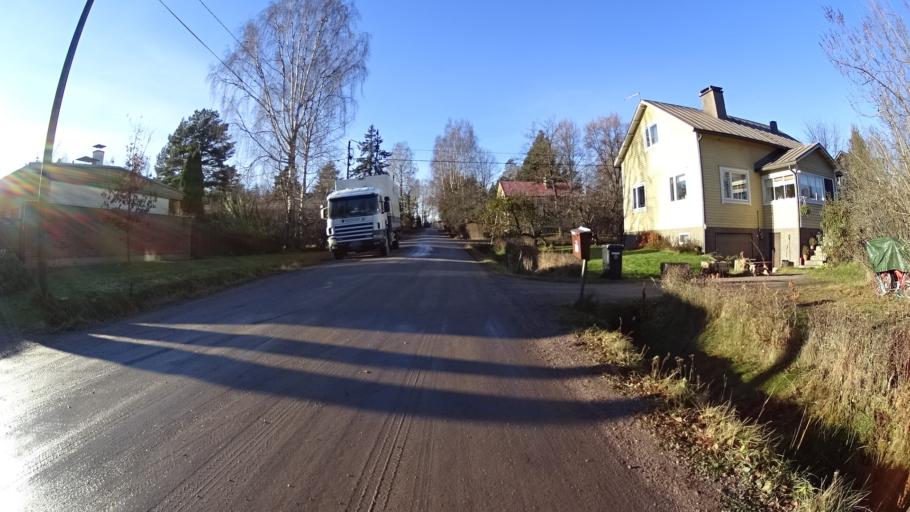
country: FI
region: Uusimaa
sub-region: Helsinki
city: Teekkarikylae
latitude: 60.2389
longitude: 24.8300
